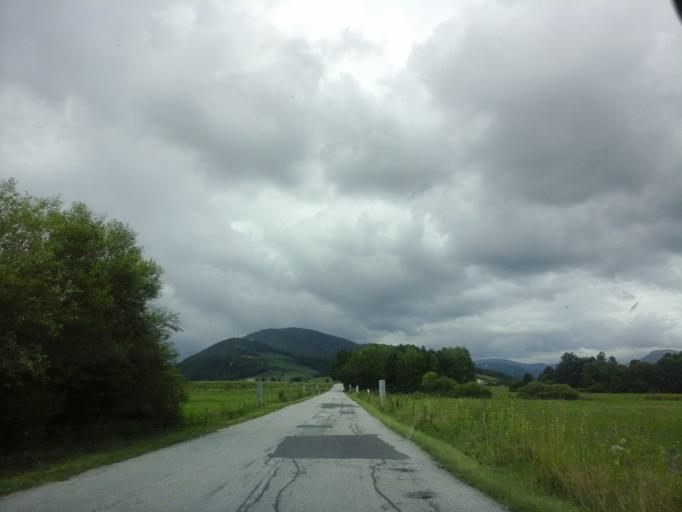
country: SK
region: Kosicky
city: Dobsina
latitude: 48.6788
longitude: 20.3544
